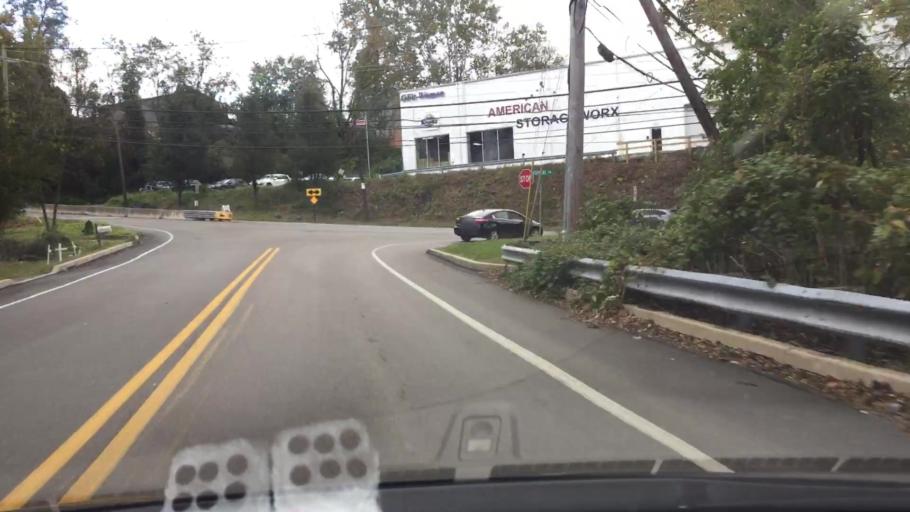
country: US
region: Pennsylvania
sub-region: Delaware County
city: Media
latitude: 39.9173
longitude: -75.4020
